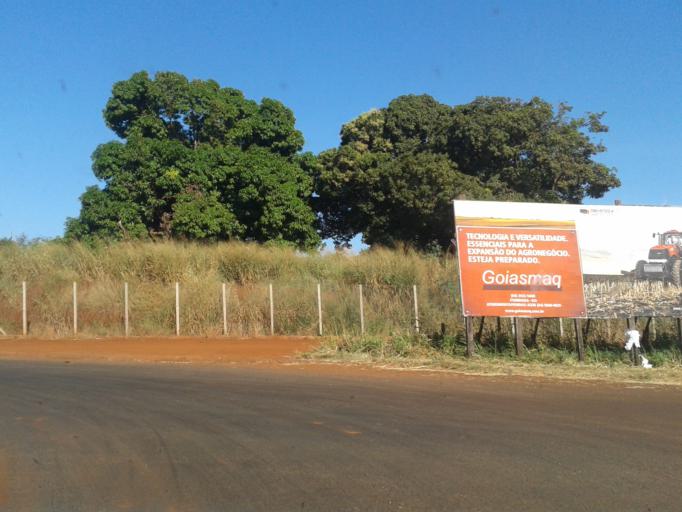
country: BR
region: Minas Gerais
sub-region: Capinopolis
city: Capinopolis
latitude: -18.6869
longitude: -49.5633
